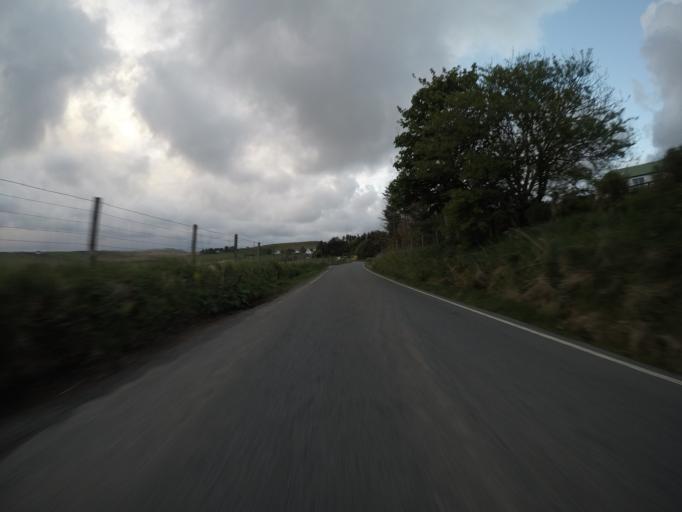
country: GB
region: Scotland
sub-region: Highland
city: Portree
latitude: 57.6149
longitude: -6.3712
